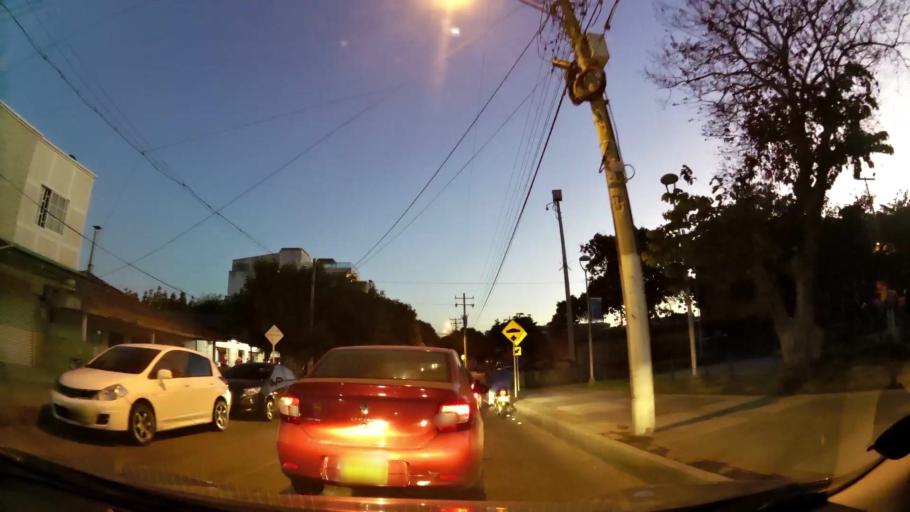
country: CO
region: Atlantico
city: Barranquilla
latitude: 10.9746
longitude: -74.8034
